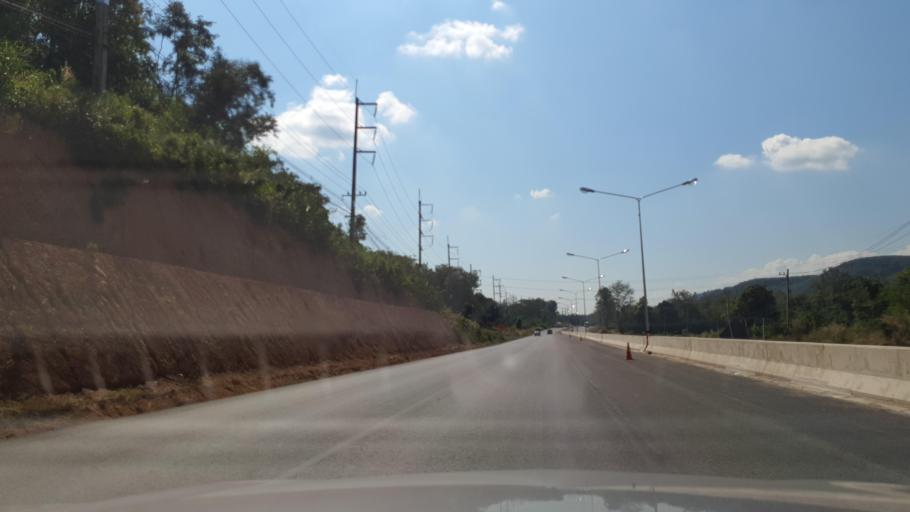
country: TH
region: Nan
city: Nan
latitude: 18.9058
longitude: 100.7605
